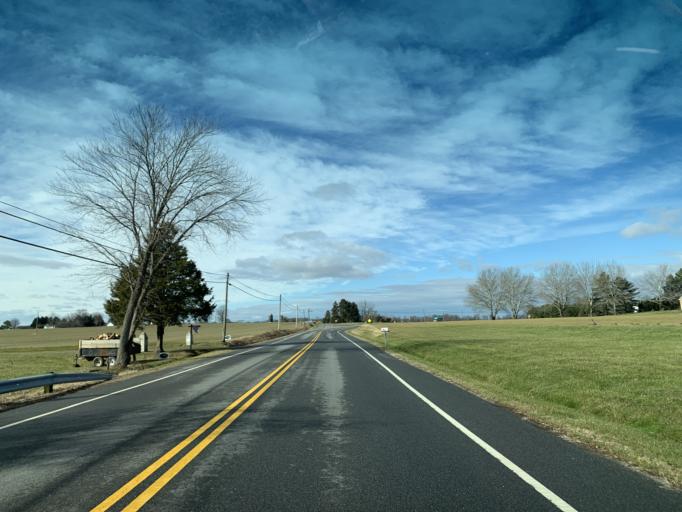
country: US
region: Maryland
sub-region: Kent County
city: Chestertown
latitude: 39.3302
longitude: -76.0576
